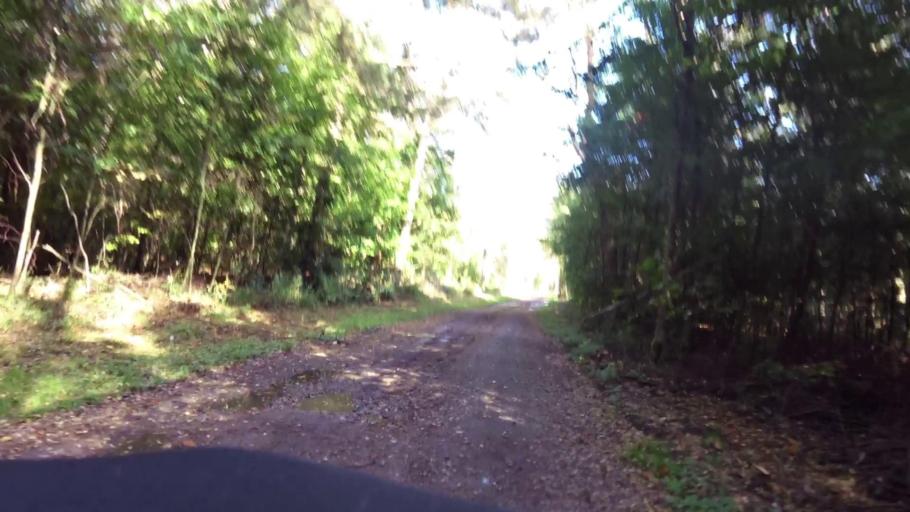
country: PL
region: West Pomeranian Voivodeship
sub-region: Powiat bialogardzki
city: Bialogard
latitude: 53.9932
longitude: 16.1143
